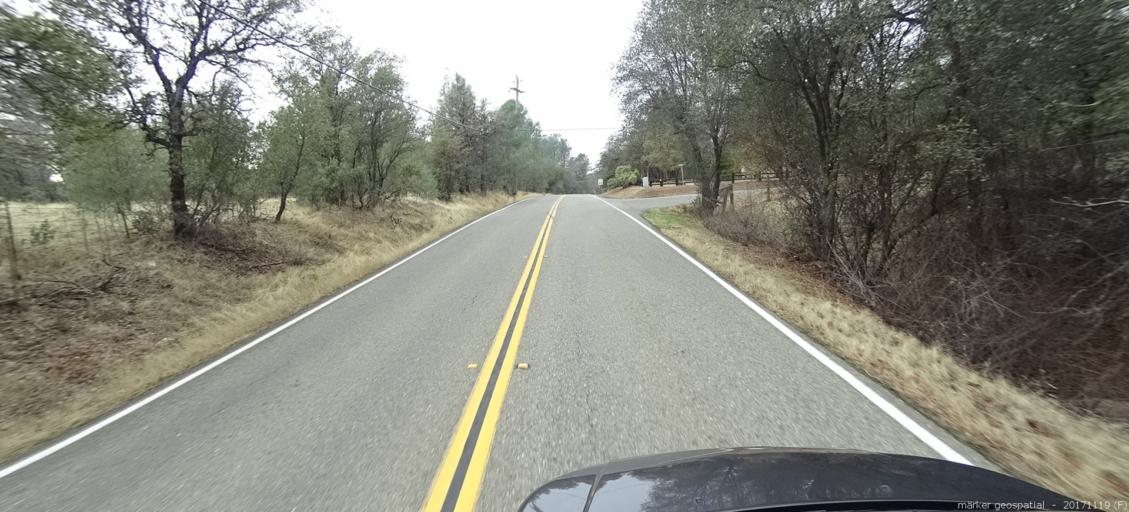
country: US
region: California
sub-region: Shasta County
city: Redding
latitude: 40.4904
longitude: -122.3998
